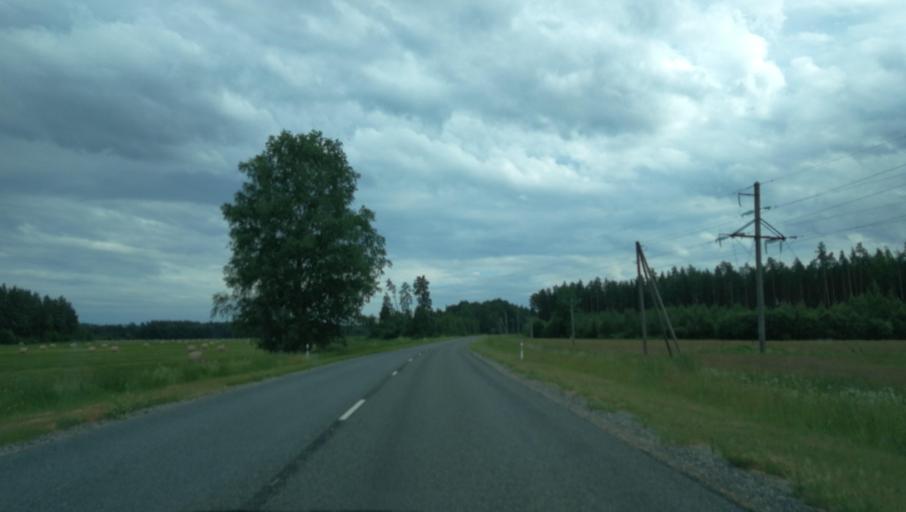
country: LV
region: Naukseni
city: Naukseni
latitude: 57.7766
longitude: 25.4306
